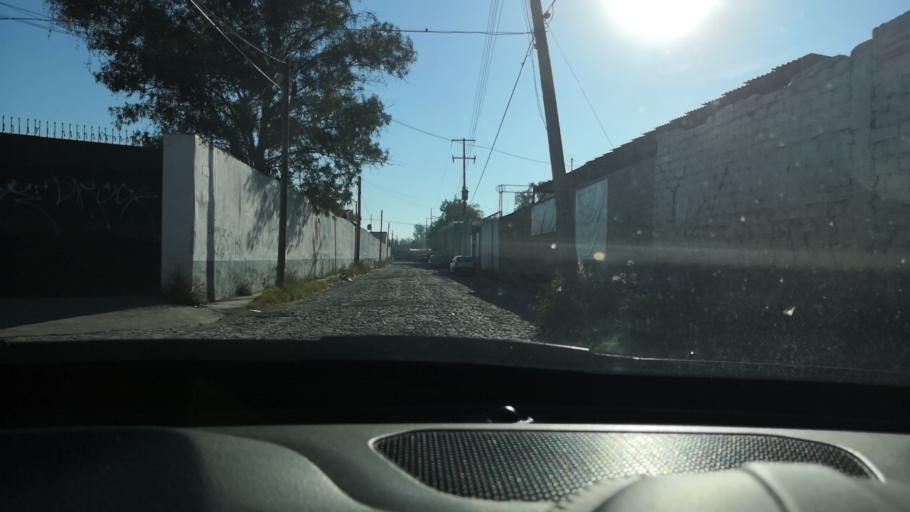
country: MX
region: Jalisco
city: Las Pintas de Arriba
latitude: 20.5931
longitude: -103.3207
